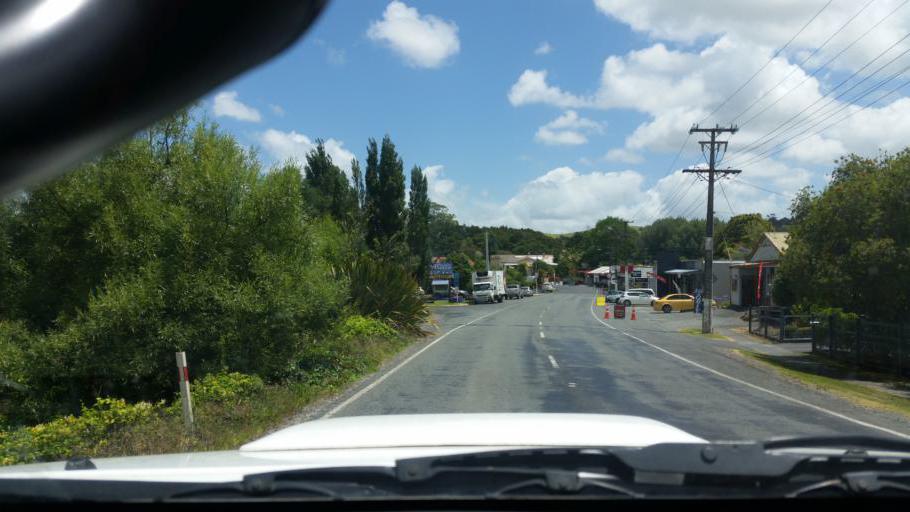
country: NZ
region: Northland
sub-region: Whangarei
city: Ruakaka
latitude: -36.0996
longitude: 174.2360
